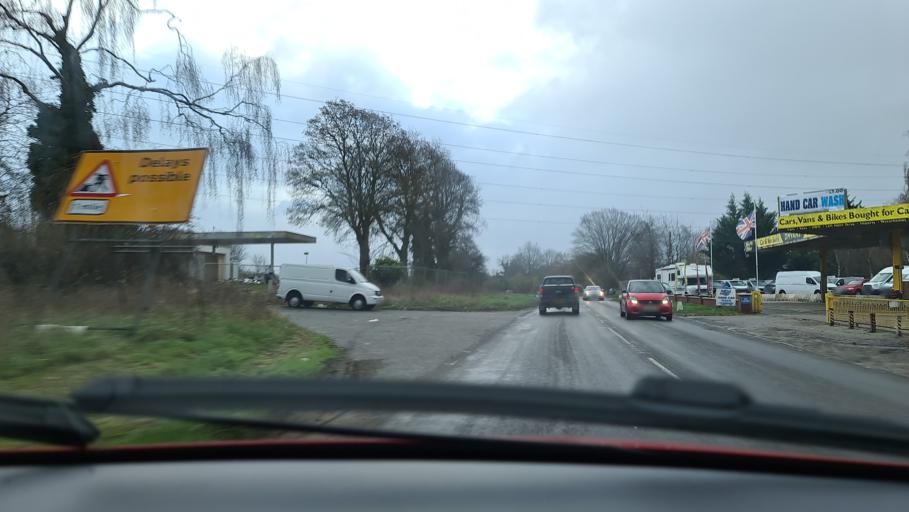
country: GB
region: England
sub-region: Buckinghamshire
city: Great Missenden
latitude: 51.6859
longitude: -0.6840
